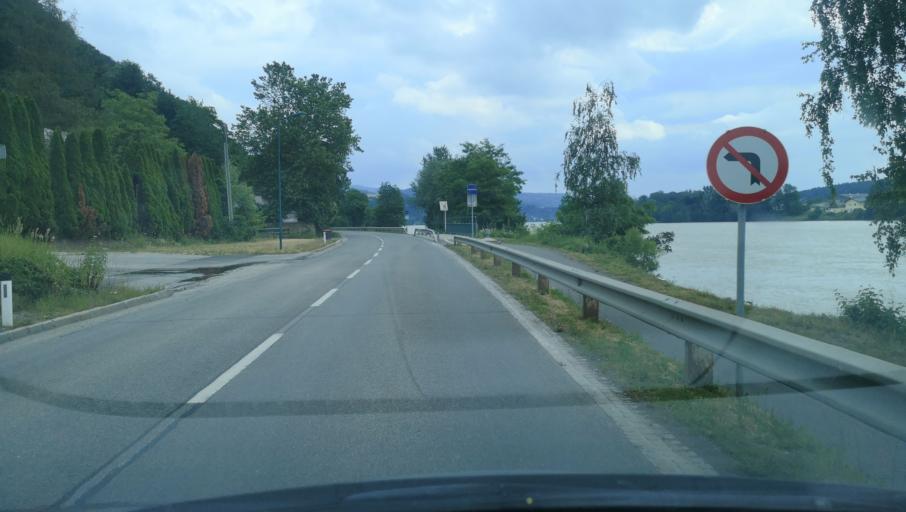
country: AT
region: Lower Austria
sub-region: Politischer Bezirk Melk
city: Marbach an der Donau
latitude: 48.2029
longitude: 15.1117
